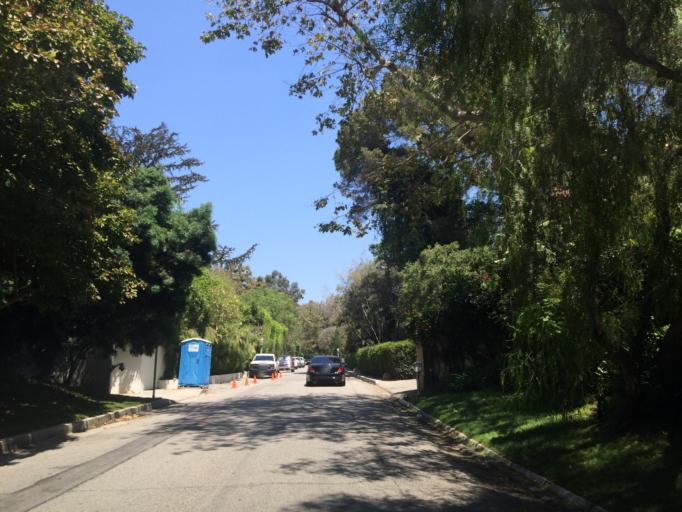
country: US
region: California
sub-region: Los Angeles County
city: Westwood, Los Angeles
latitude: 34.0878
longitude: -118.4464
